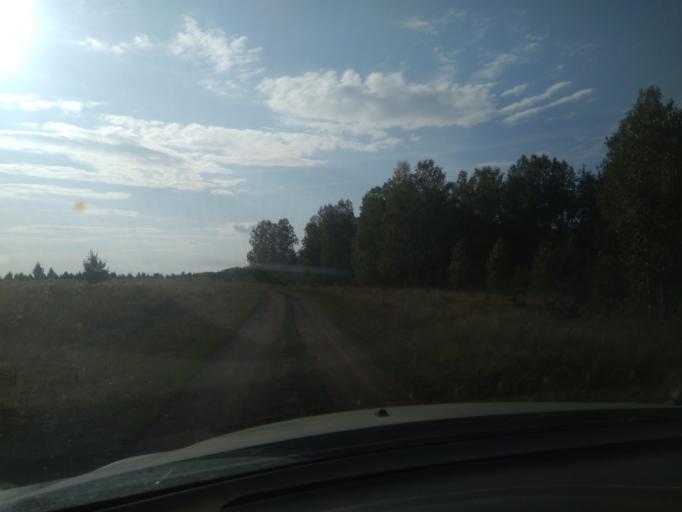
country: RU
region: Sverdlovsk
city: Pokrovskoye
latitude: 56.4298
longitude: 61.6063
